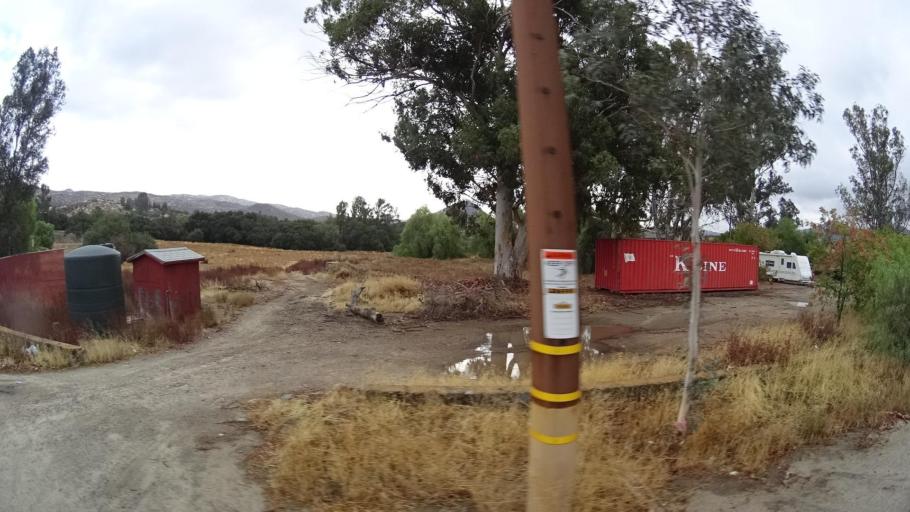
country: MX
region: Baja California
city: Tecate
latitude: 32.5806
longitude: -116.6214
